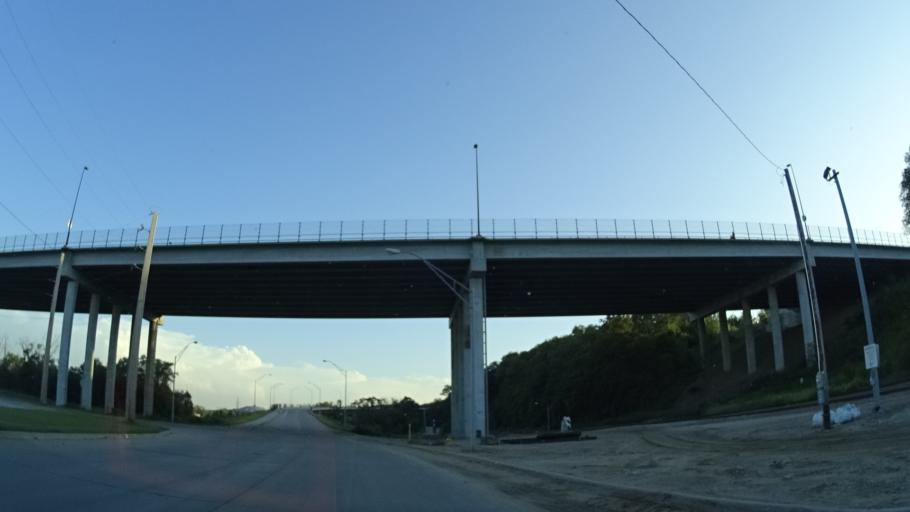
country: US
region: Nebraska
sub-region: Douglas County
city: Omaha
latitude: 41.2136
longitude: -95.9314
